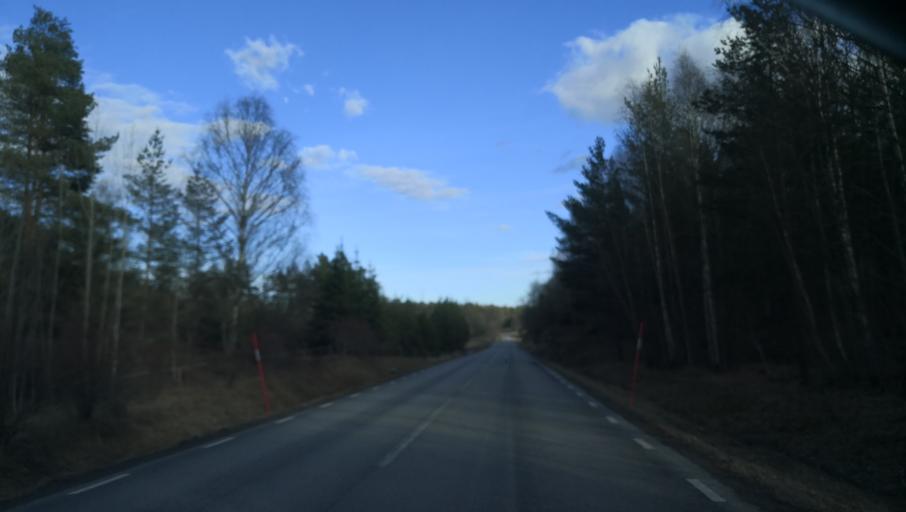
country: SE
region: Stockholm
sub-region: Varmdo Kommun
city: Gustavsberg
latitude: 59.3488
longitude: 18.3735
